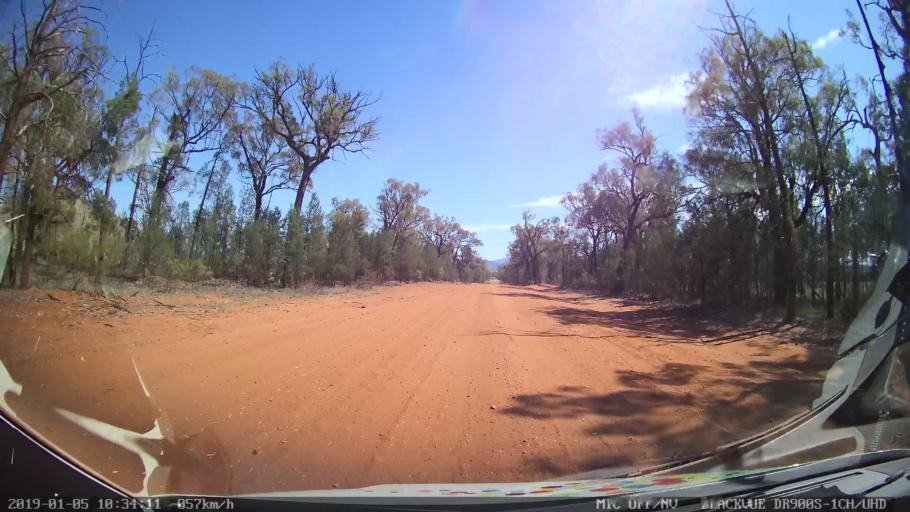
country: AU
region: New South Wales
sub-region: Gilgandra
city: Gilgandra
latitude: -31.5003
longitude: 148.9290
